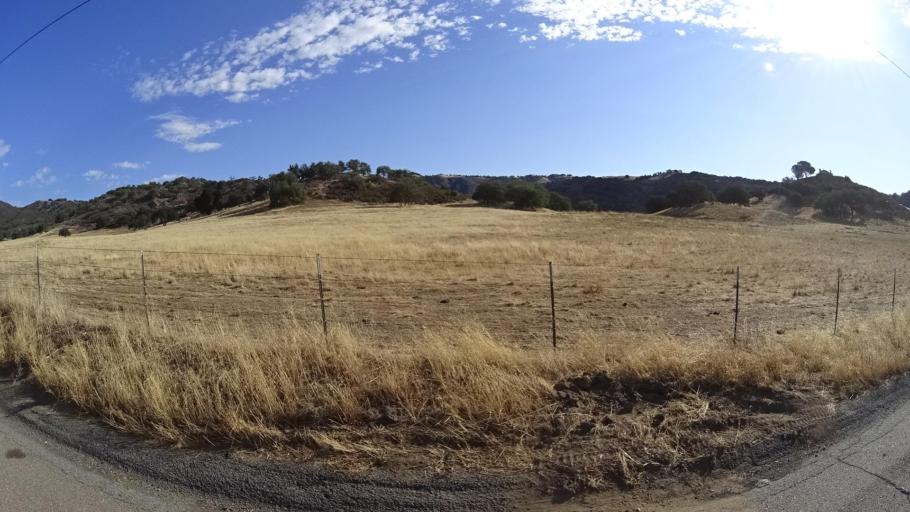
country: US
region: California
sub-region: San Diego County
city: Julian
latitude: 33.1407
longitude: -116.6860
